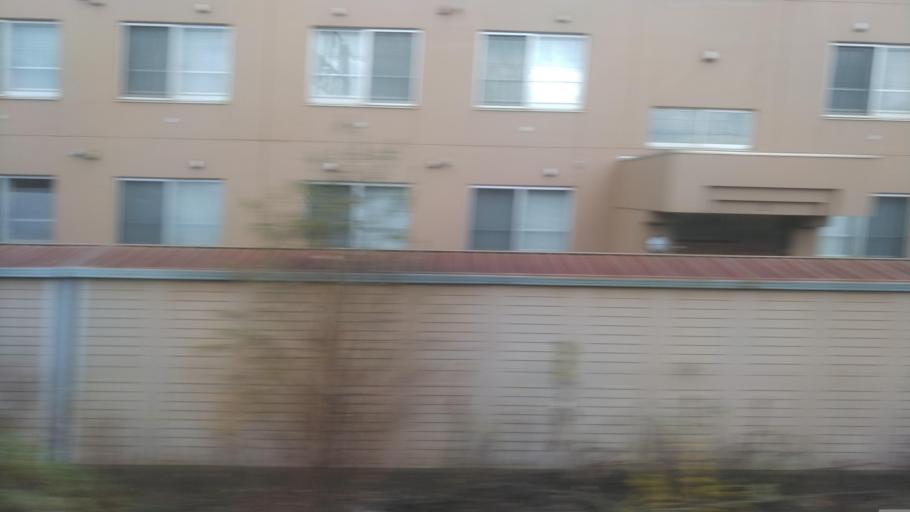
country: JP
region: Hokkaido
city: Chitose
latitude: 42.8841
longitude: 141.5852
